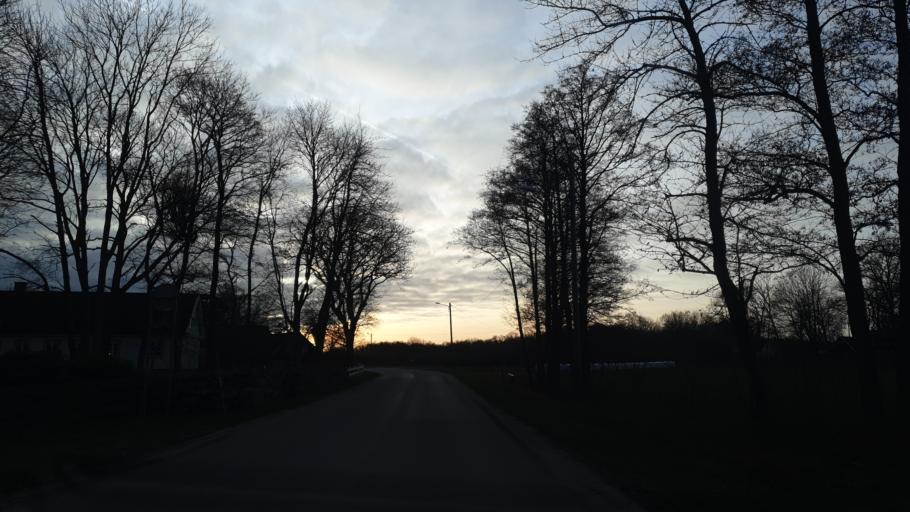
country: SE
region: Blekinge
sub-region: Karlskrona Kommun
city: Jaemjoe
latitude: 56.1516
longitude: 15.9038
